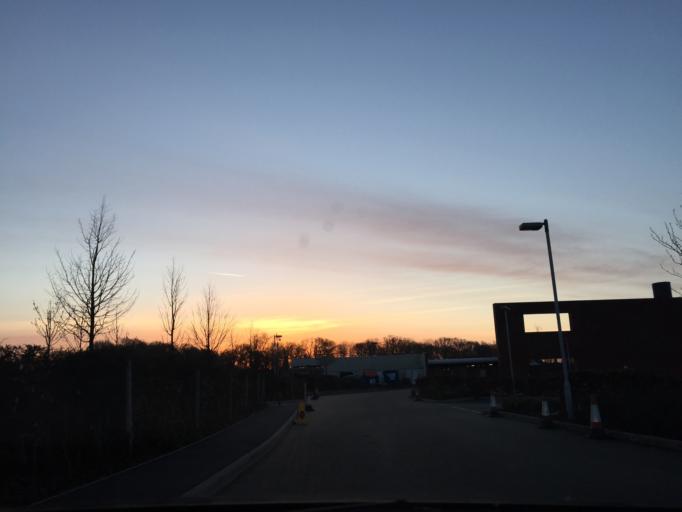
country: GB
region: England
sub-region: Hampshire
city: Totton
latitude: 50.9391
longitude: -1.4719
